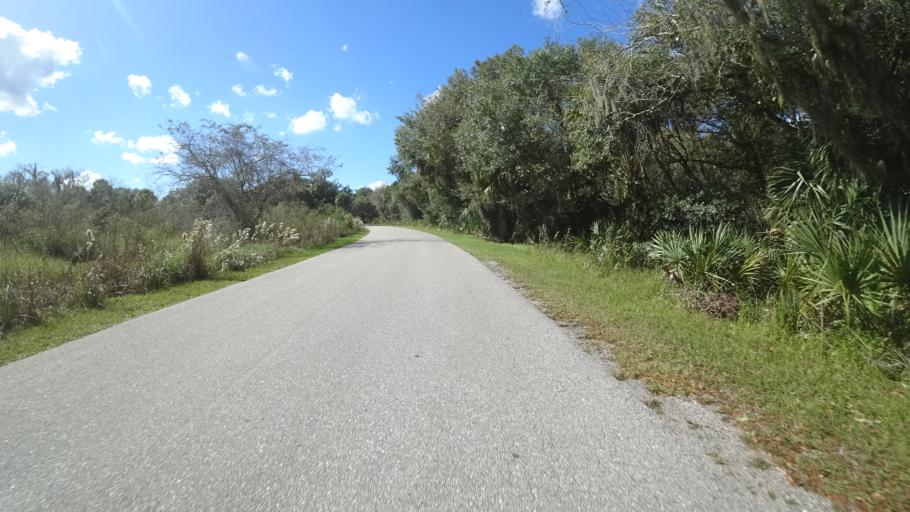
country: US
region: Florida
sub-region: Sarasota County
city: Lake Sarasota
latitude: 27.2464
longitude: -82.3105
